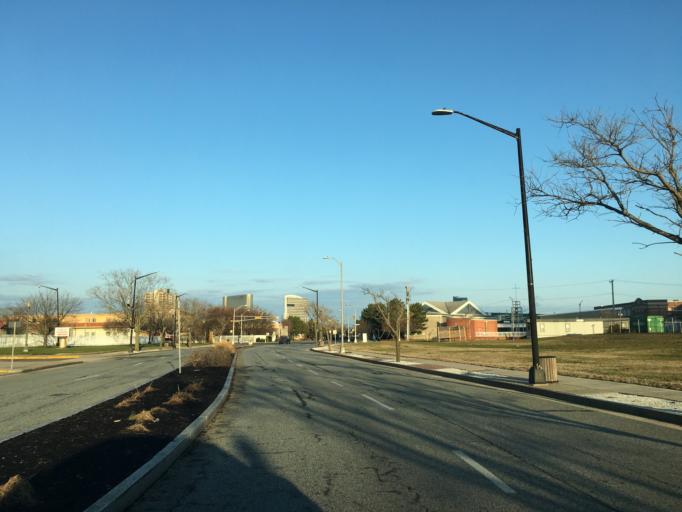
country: US
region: New Jersey
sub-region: Atlantic County
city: Atlantic City
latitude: 39.3642
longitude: -74.4196
